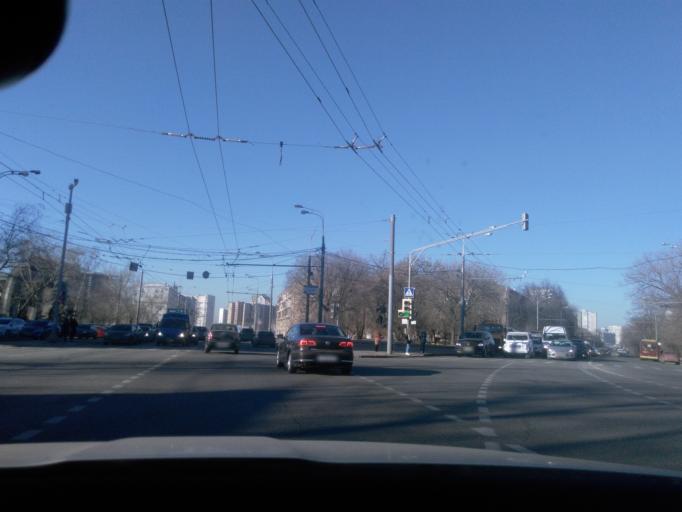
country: RU
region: Moscow
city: Sokol
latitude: 55.7763
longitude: 37.5035
